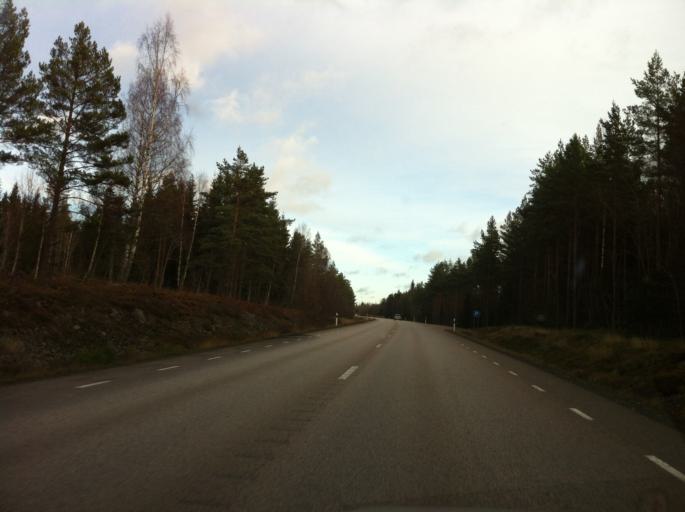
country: SE
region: Kronoberg
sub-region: Uppvidinge Kommun
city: Aseda
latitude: 57.1564
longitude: 15.3220
